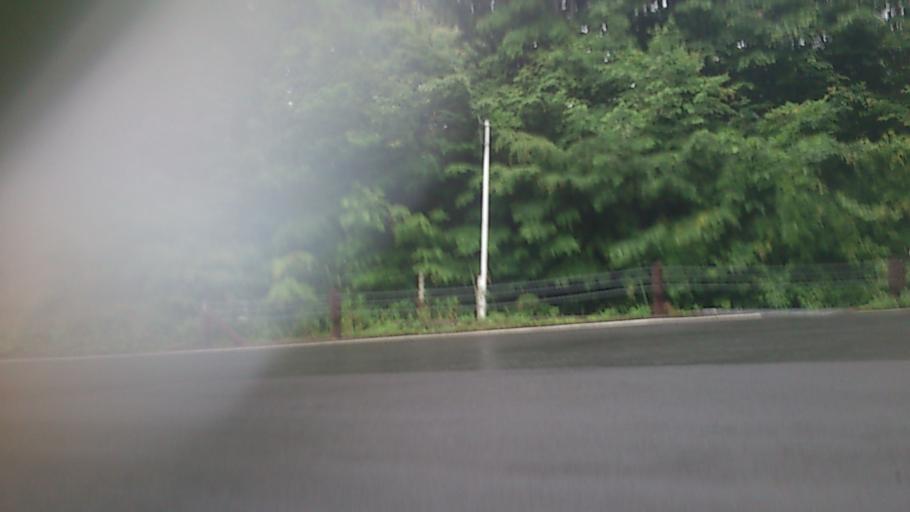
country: JP
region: Akita
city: Noshiromachi
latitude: 40.5613
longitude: 139.9630
